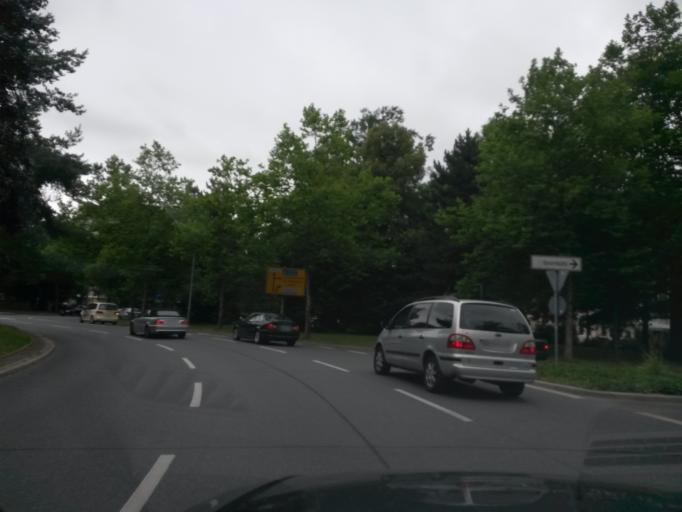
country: DE
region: Bavaria
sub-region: Regierungsbezirk Unterfranken
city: Wuerzburg
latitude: 49.7988
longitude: 9.9430
